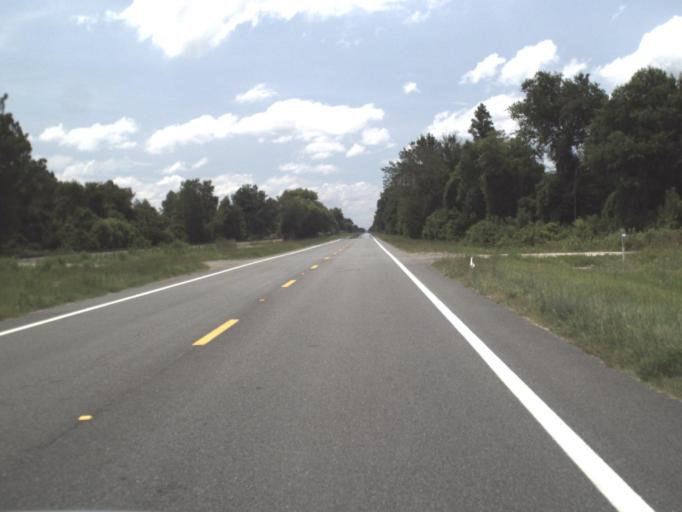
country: US
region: Florida
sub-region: Hamilton County
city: Jasper
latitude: 30.4596
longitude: -82.8957
